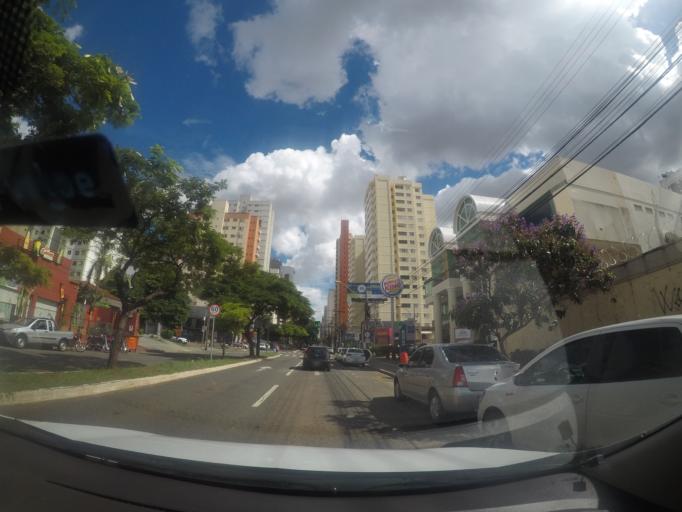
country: BR
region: Goias
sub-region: Goiania
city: Goiania
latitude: -16.7103
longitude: -49.2671
